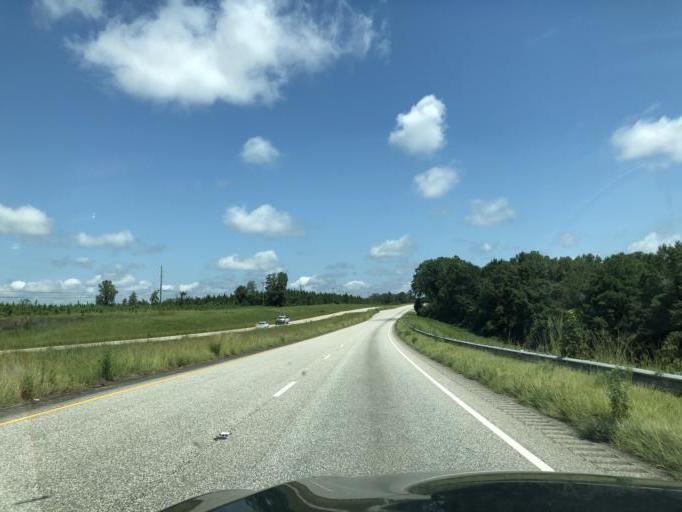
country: US
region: Alabama
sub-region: Henry County
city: Abbeville
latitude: 31.7133
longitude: -85.2727
